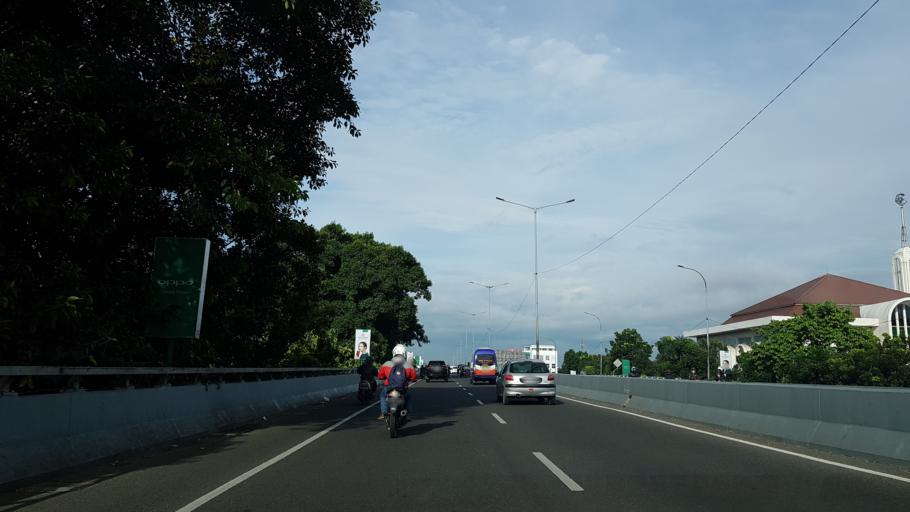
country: ID
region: West Java
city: Bandung
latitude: -6.9004
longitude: 107.6006
